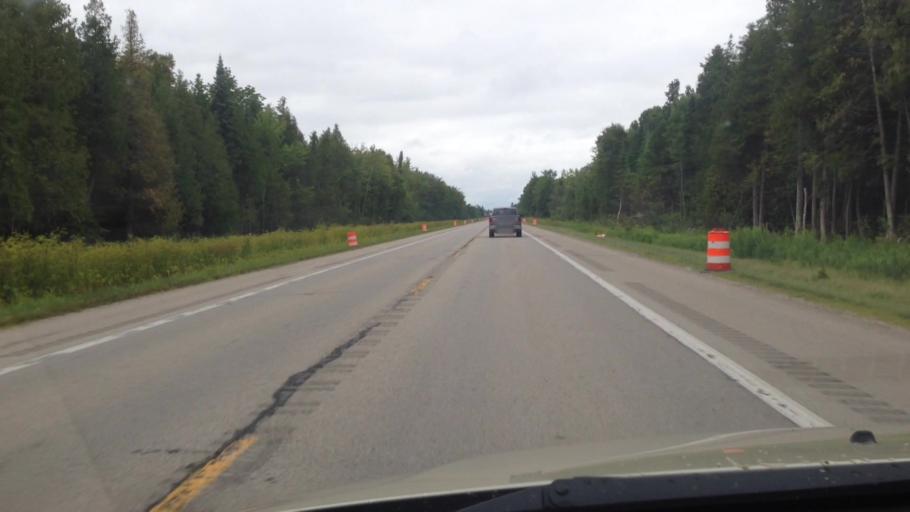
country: US
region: Michigan
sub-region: Delta County
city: Escanaba
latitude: 45.6020
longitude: -87.2242
